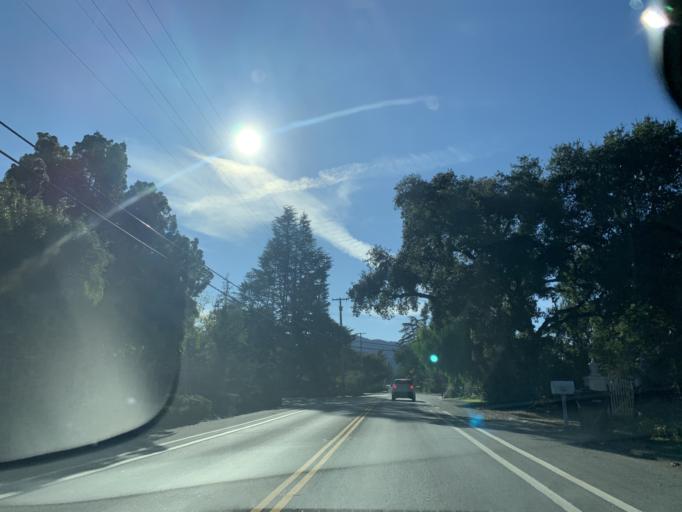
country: US
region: California
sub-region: Santa Clara County
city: Los Altos
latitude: 37.3782
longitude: -122.1037
